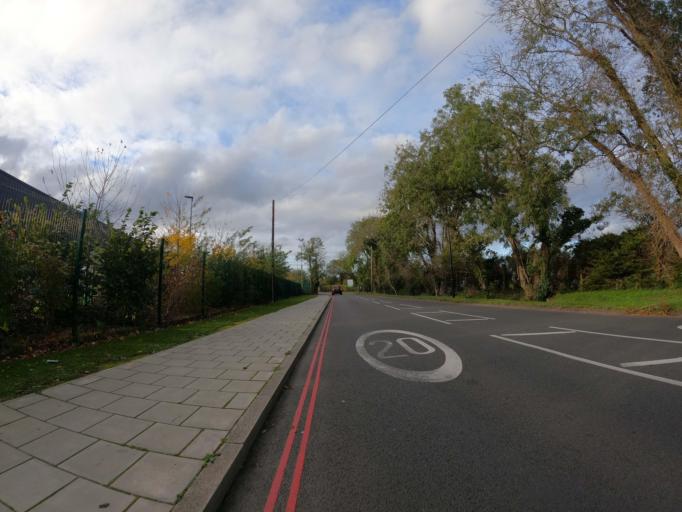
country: GB
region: England
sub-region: Greater London
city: Isleworth
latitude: 51.4875
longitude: -0.3363
